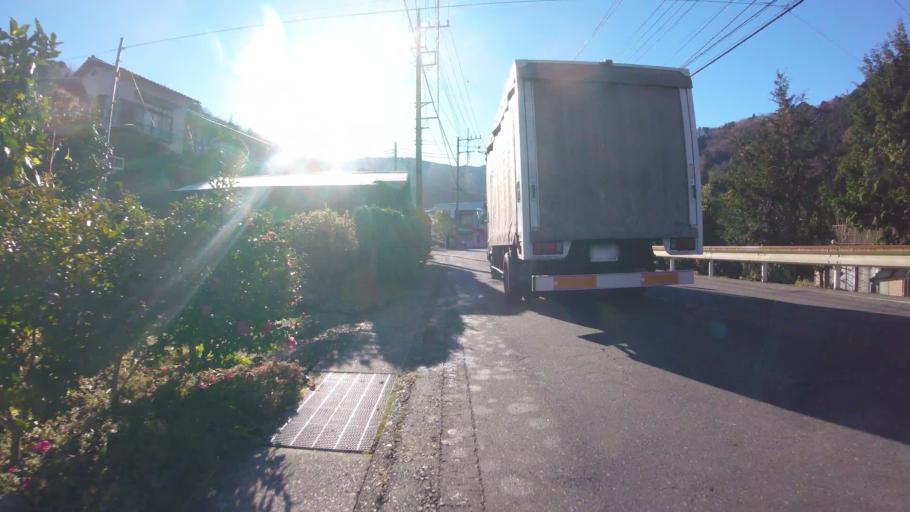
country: JP
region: Shizuoka
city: Heda
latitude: 34.8881
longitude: 138.9299
